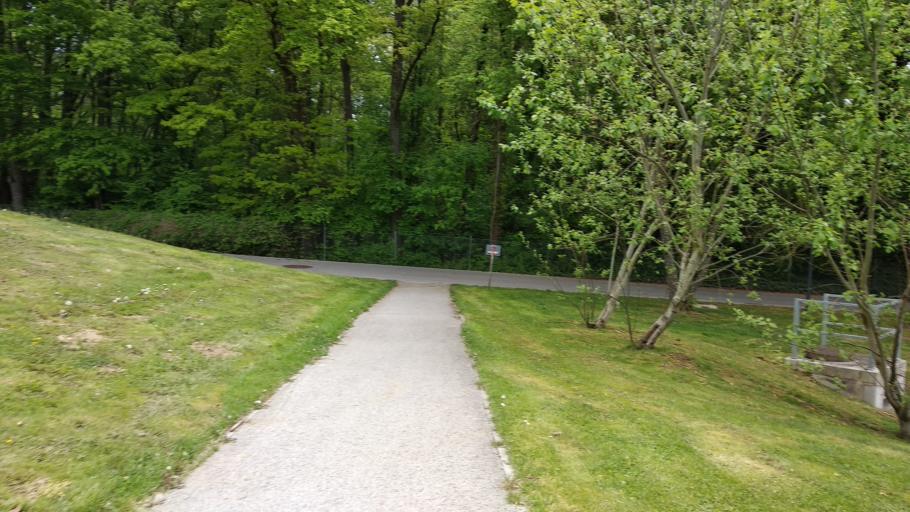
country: DE
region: Bavaria
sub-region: Upper Bavaria
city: Freising
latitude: 48.4015
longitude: 11.7246
